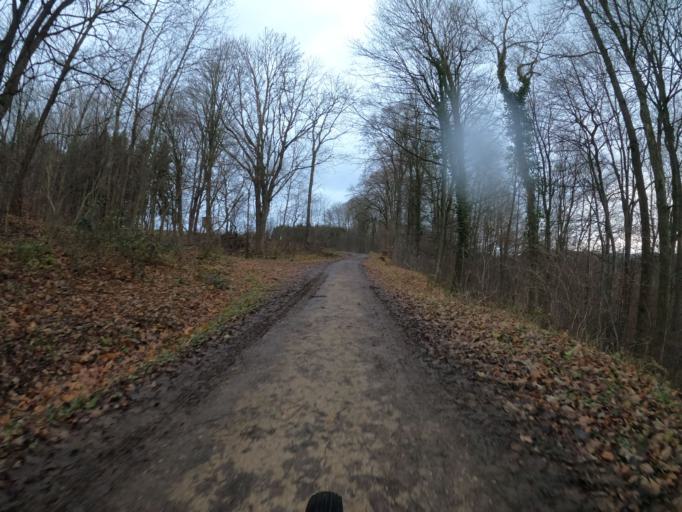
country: DE
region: Baden-Wuerttemberg
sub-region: Regierungsbezirk Stuttgart
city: Sussen
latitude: 48.7000
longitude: 9.7715
